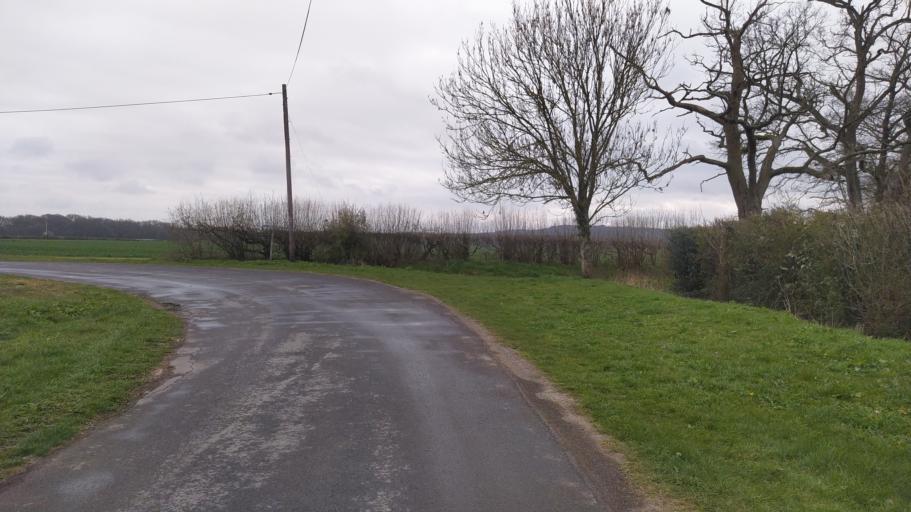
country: GB
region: England
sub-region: West Sussex
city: Petworth
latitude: 51.0246
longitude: -0.5809
